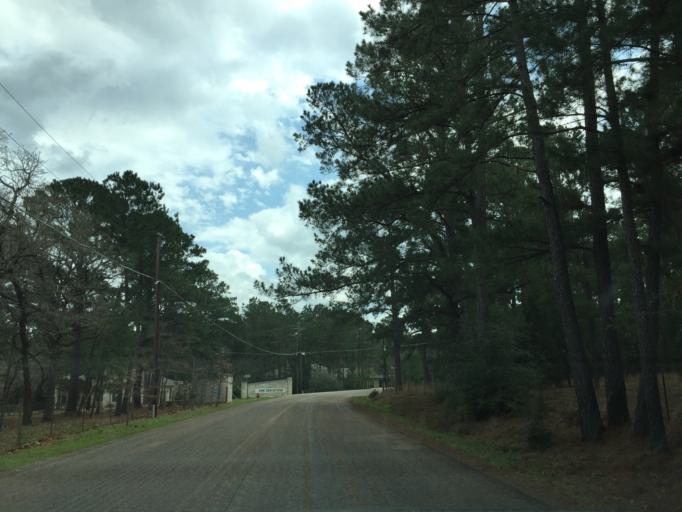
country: US
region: Texas
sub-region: Bastrop County
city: Bastrop
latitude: 30.1264
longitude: -97.2807
